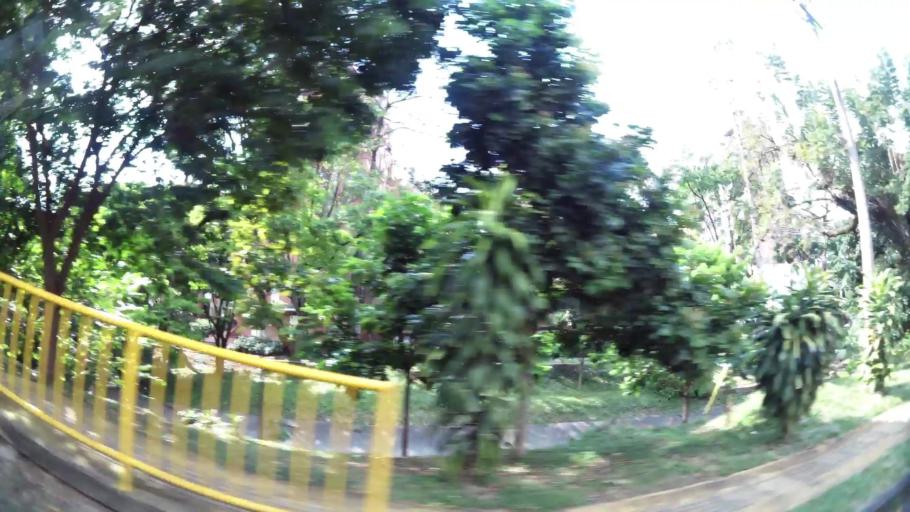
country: CO
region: Antioquia
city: Medellin
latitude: 6.2405
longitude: -75.5842
